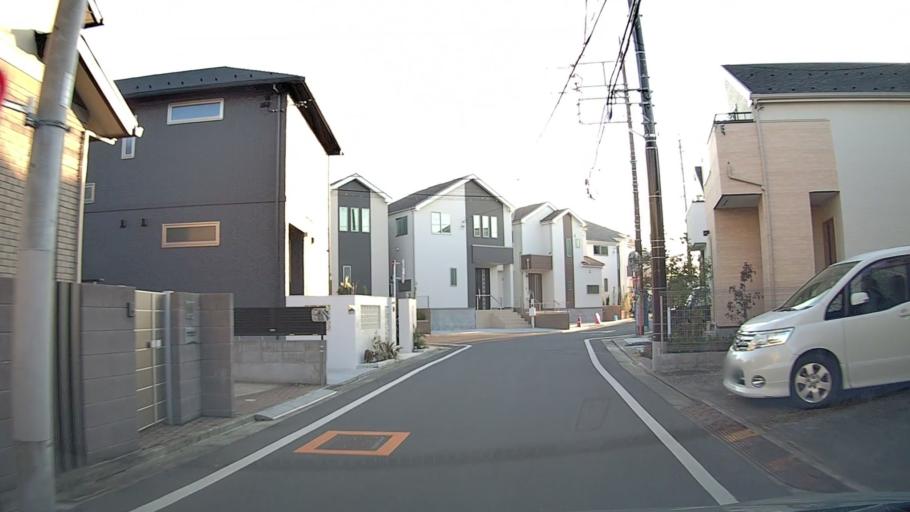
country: JP
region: Saitama
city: Wako
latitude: 35.7685
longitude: 139.6161
